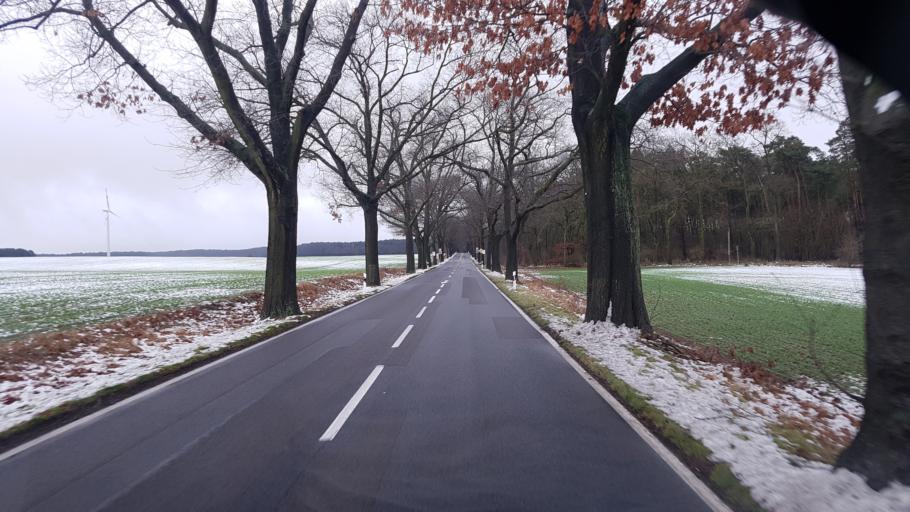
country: DE
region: Brandenburg
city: Schenkendobern
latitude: 51.9663
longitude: 14.5867
